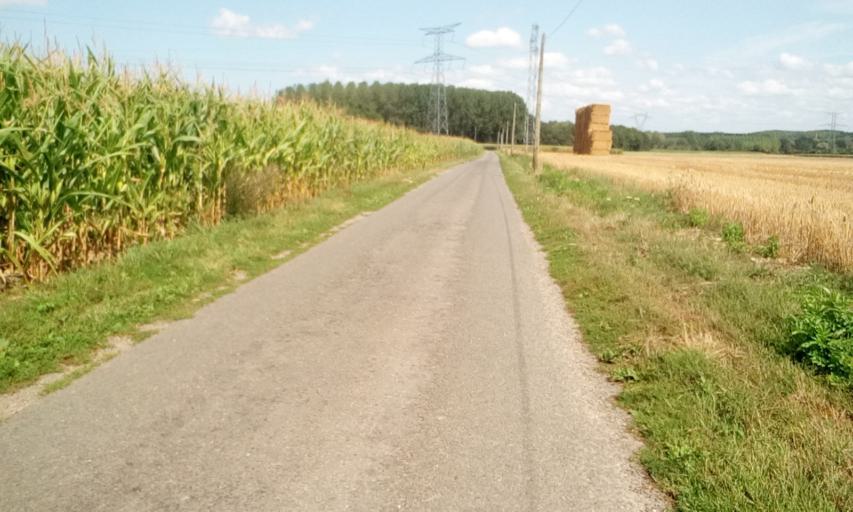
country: FR
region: Lower Normandy
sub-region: Departement du Calvados
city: Bellengreville
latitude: 49.1314
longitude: -0.1893
